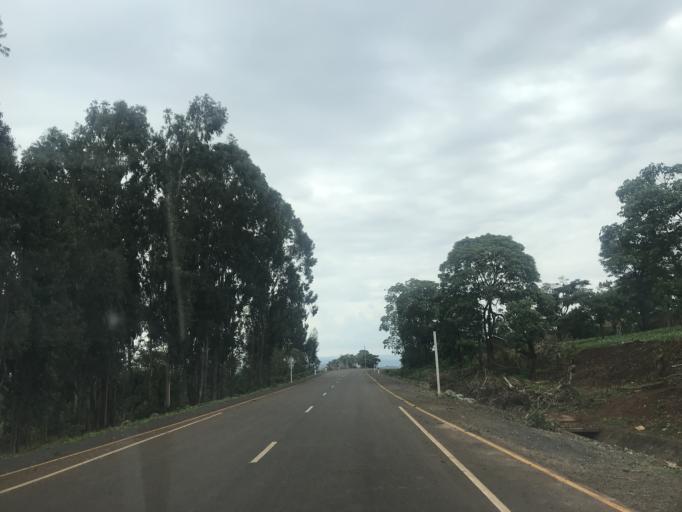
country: ET
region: Oromiya
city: Shambu
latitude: 9.8686
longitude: 36.6869
